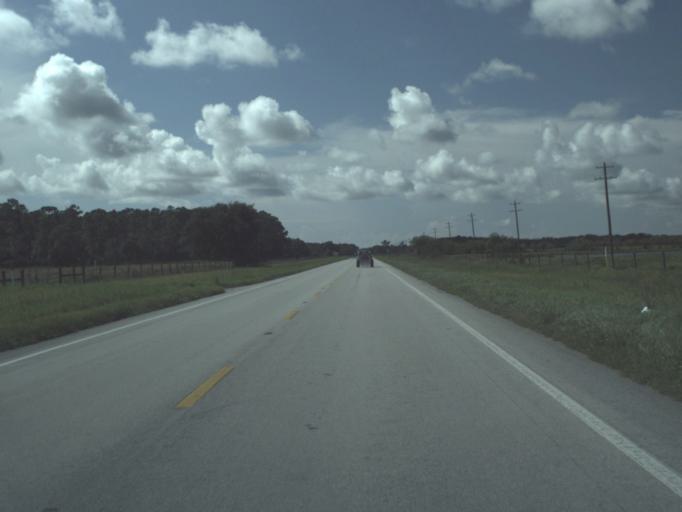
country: US
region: Florida
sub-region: Okeechobee County
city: Cypress Quarters
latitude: 27.3151
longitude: -80.8254
